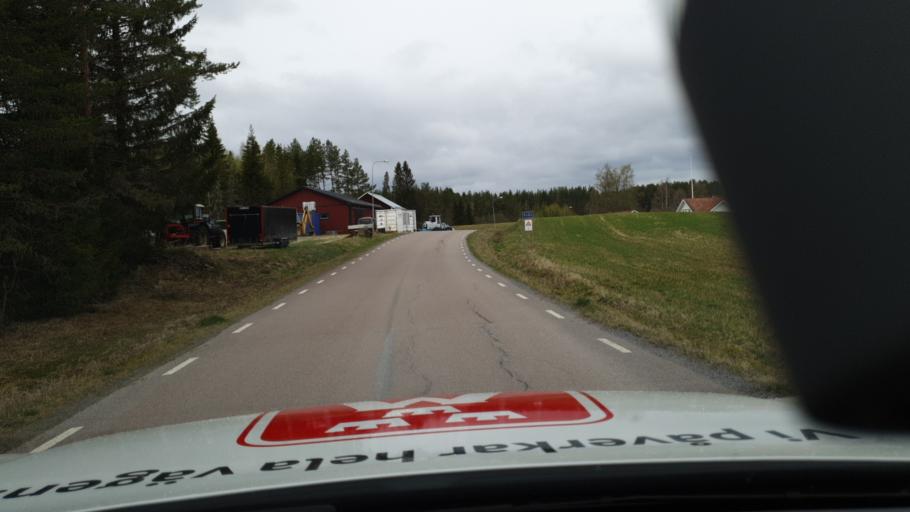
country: SE
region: Jaemtland
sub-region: OEstersunds Kommun
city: Lit
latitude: 63.2936
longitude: 14.9841
